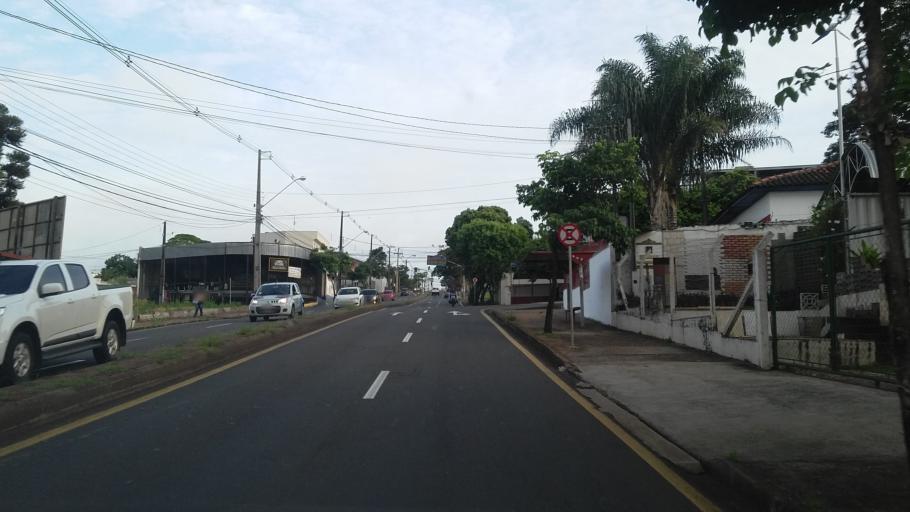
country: BR
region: Parana
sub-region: Londrina
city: Londrina
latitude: -23.3234
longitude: -51.1761
